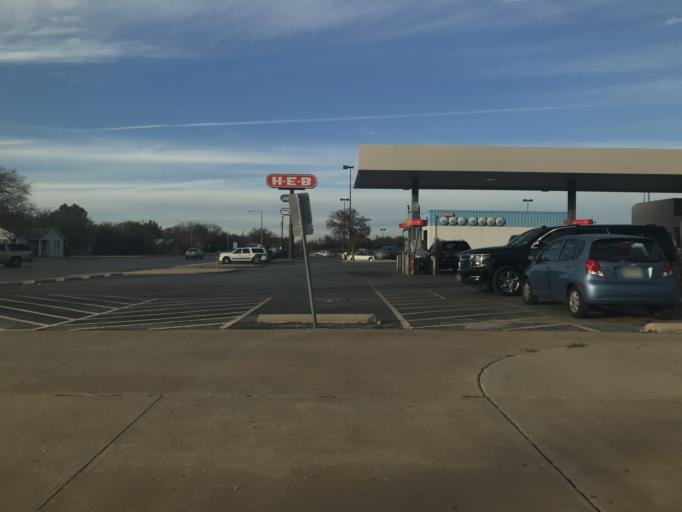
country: US
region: Texas
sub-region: Taylor County
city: Abilene
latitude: 32.4323
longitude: -99.7592
